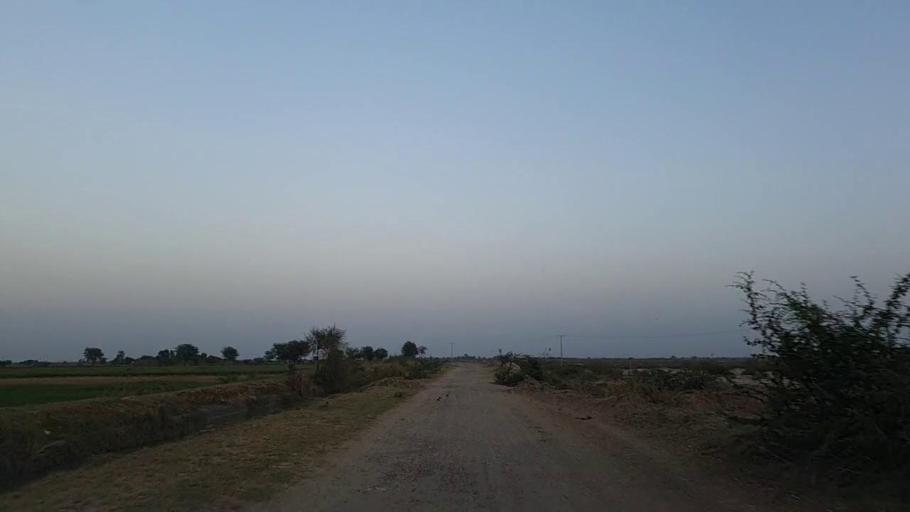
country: PK
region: Sindh
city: Pithoro
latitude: 25.4146
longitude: 69.3129
